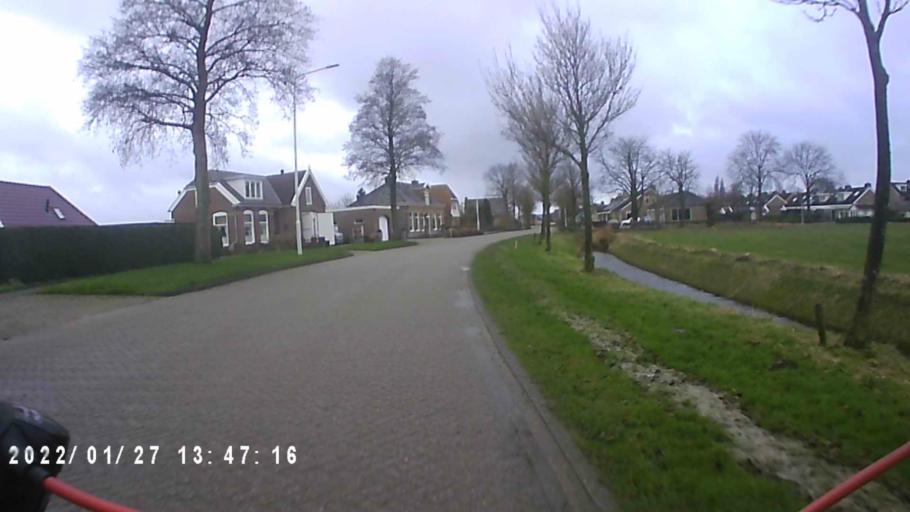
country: NL
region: Friesland
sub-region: Gemeente Kollumerland en Nieuwkruisland
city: Kollum
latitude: 53.3027
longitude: 6.1937
